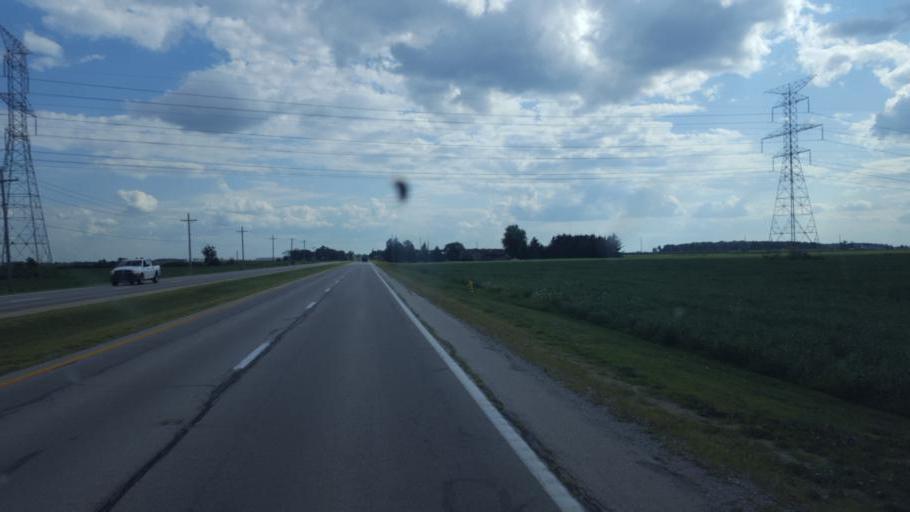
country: US
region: Ohio
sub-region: Wood County
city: Haskins
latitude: 41.4759
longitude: -83.6473
